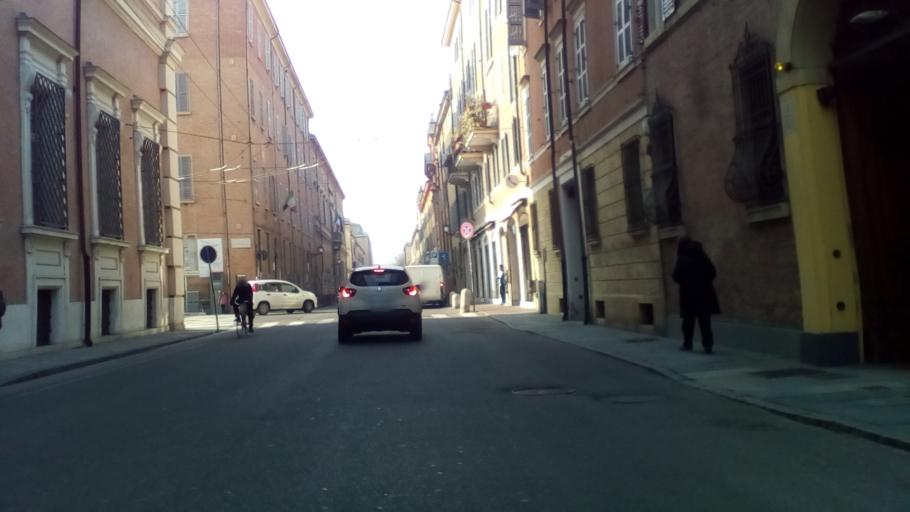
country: IT
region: Emilia-Romagna
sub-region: Provincia di Modena
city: Modena
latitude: 44.6495
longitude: 10.9293
